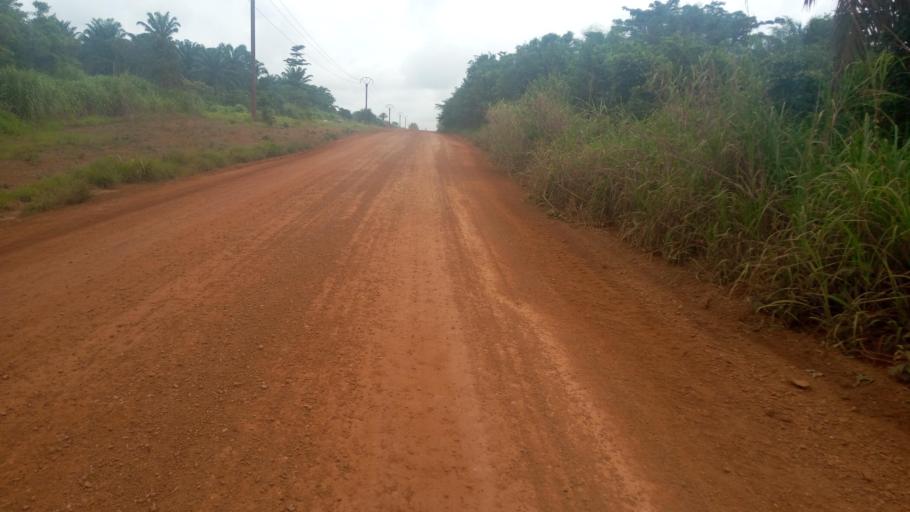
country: SL
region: Southern Province
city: Mogbwemo
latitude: 7.7136
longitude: -12.2851
